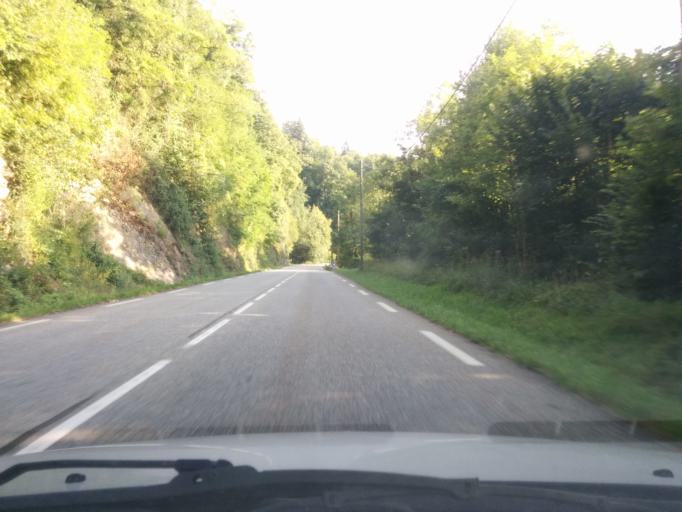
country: FR
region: Rhone-Alpes
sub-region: Departement de la Savoie
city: Saint-Beron
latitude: 45.4868
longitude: 5.7213
